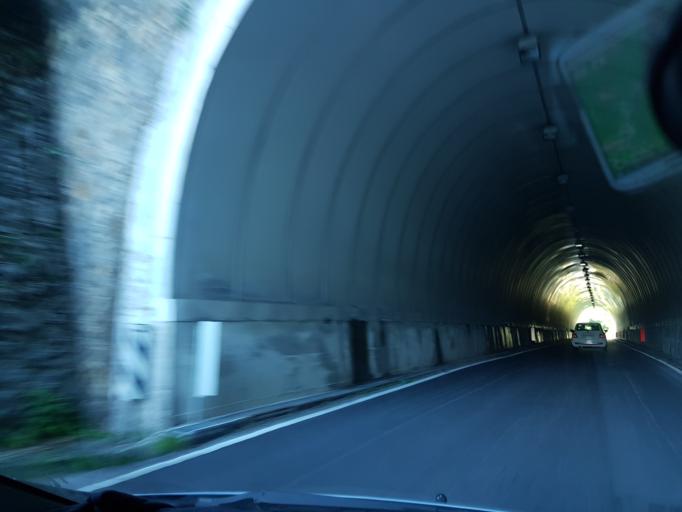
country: IT
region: Tuscany
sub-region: Provincia di Lucca
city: Minucciano
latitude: 44.1644
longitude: 10.2128
